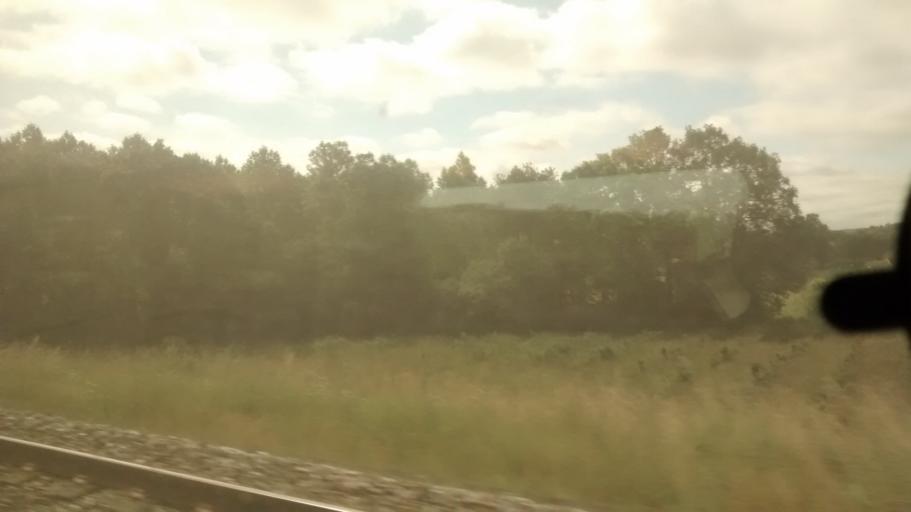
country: FR
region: Pays de la Loire
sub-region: Departement de la Sarthe
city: Vibraye
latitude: 48.0826
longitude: 0.7271
